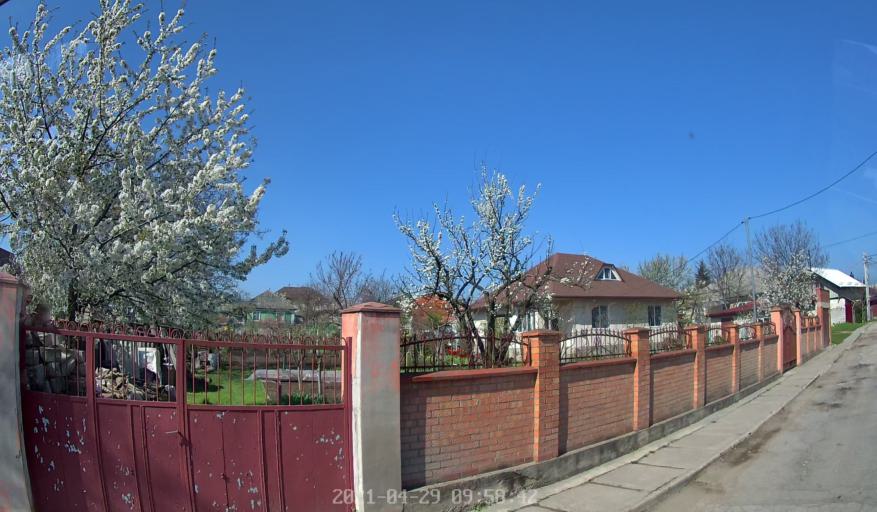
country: MD
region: Chisinau
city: Cricova
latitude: 47.1420
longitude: 28.8597
